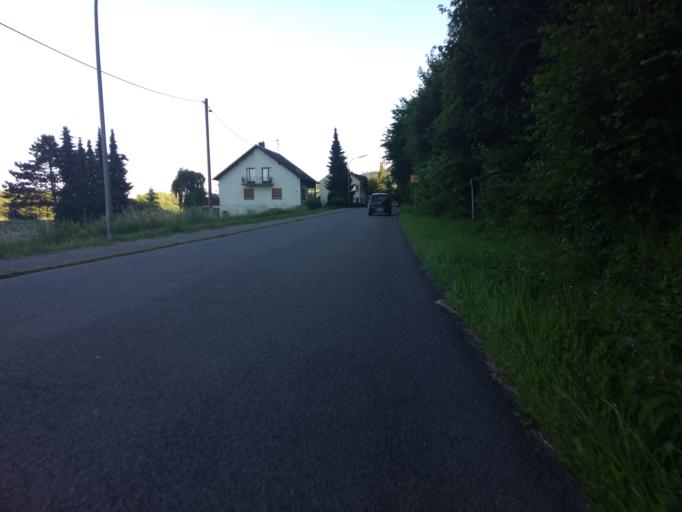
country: DE
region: Saarland
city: Merzig
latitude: 49.4251
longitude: 6.6299
